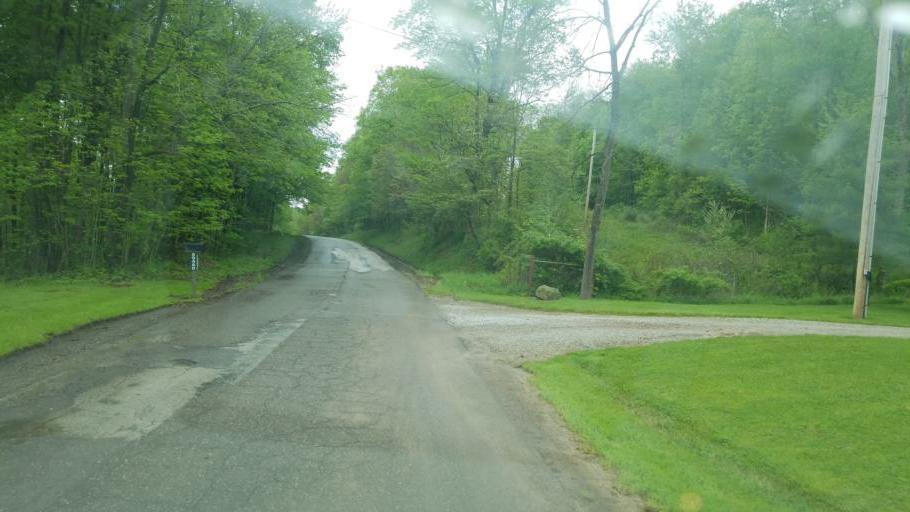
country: US
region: Ohio
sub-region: Tuscarawas County
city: Dennison
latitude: 40.3969
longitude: -81.2073
